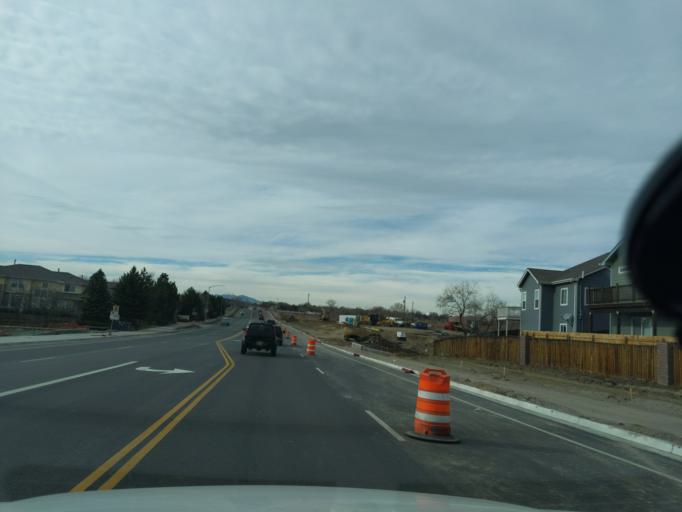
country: US
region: Colorado
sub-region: Adams County
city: Thornton
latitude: 39.8994
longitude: -104.9488
